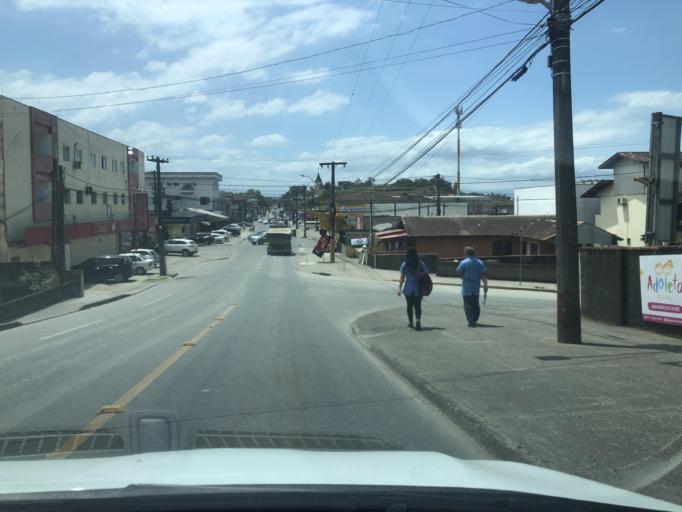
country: BR
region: Santa Catarina
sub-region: Joinville
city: Joinville
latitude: -26.3478
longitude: -48.7901
